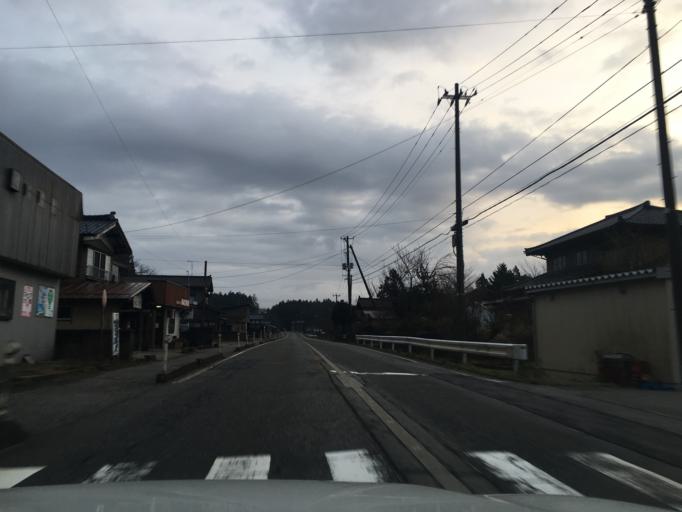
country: JP
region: Niigata
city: Murakami
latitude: 38.2951
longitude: 139.5317
